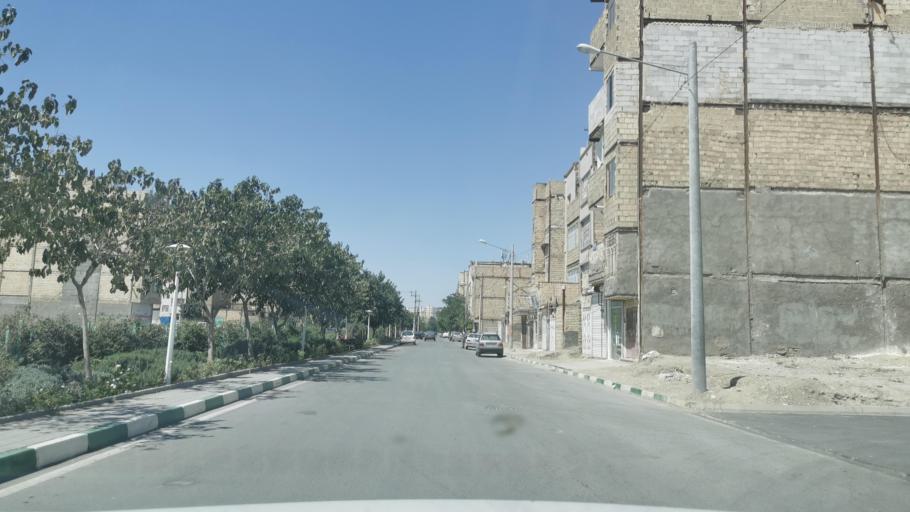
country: IR
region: Razavi Khorasan
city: Mashhad
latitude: 36.3584
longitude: 59.5631
